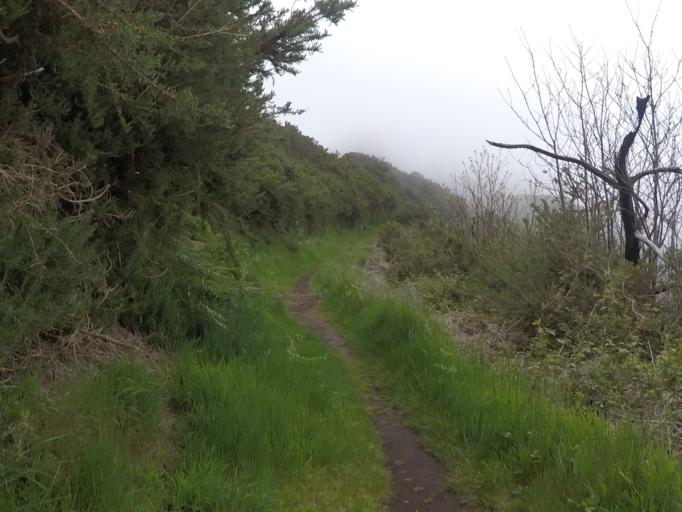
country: PT
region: Madeira
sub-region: Camara de Lobos
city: Curral das Freiras
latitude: 32.7310
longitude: -16.9858
